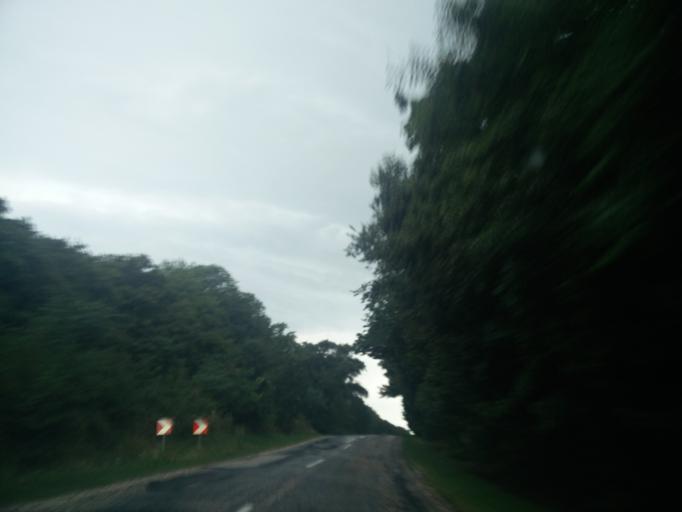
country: HU
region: Fejer
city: Pazmand
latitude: 47.2643
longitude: 18.6008
